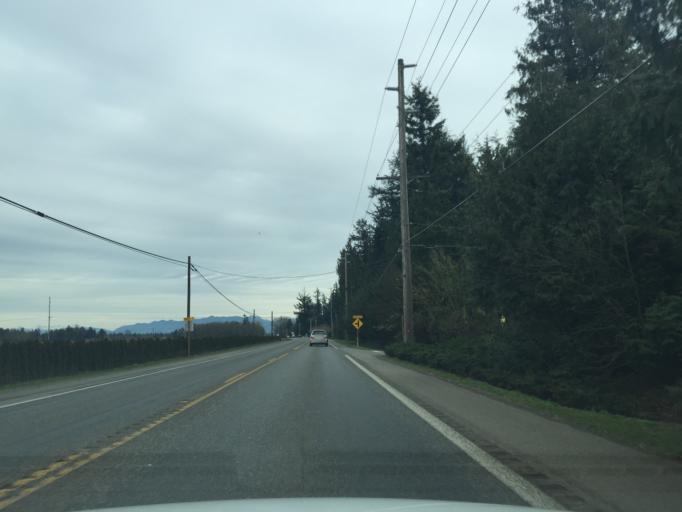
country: US
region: Washington
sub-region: Whatcom County
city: Lynden
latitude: 48.9350
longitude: -122.5106
